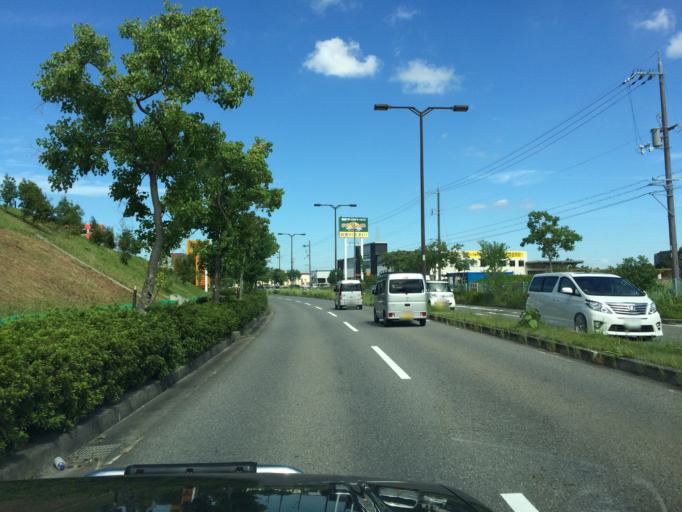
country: JP
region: Osaka
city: Izumi
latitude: 34.4393
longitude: 135.4499
